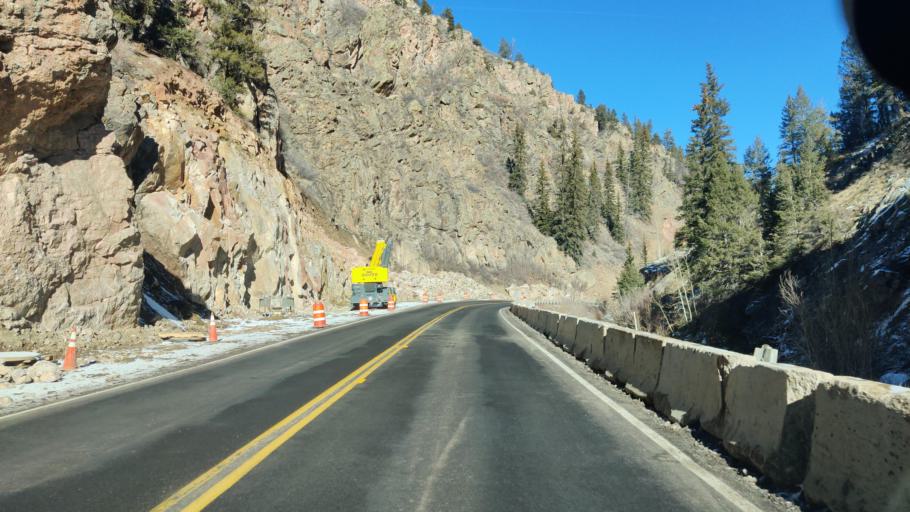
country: US
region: Colorado
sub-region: Hinsdale County
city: Lake City
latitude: 38.4012
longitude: -107.4124
